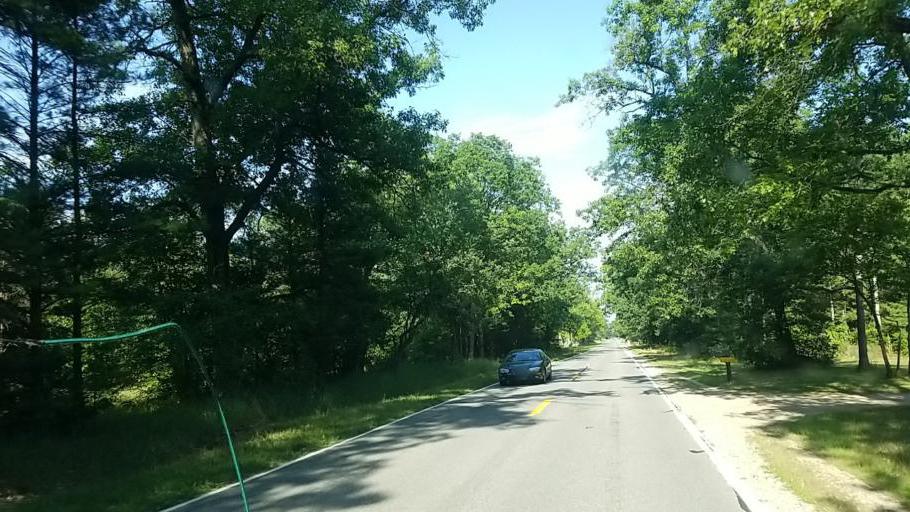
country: US
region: Michigan
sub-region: Muskegon County
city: Twin Lake
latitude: 43.4685
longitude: -86.1467
